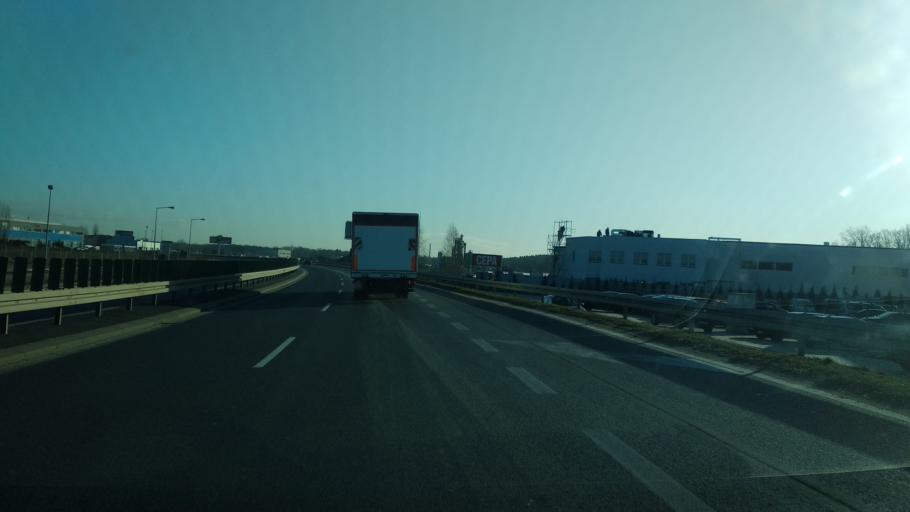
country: PL
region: Lower Silesian Voivodeship
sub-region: Powiat wroclawski
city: Dlugoleka
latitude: 51.1826
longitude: 17.2162
